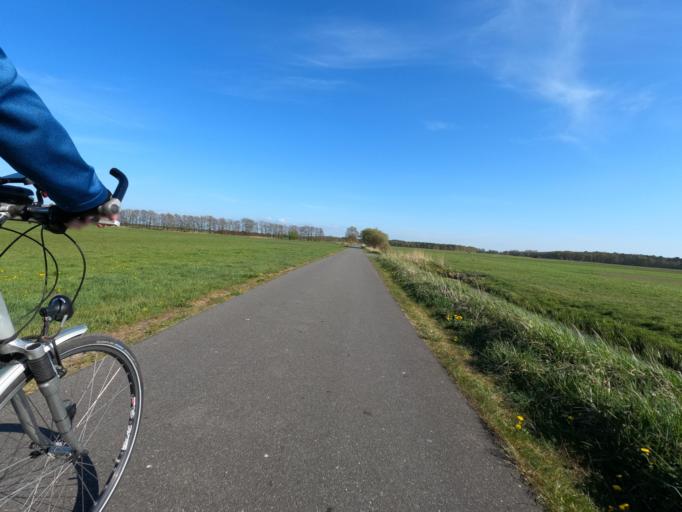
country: DE
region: Mecklenburg-Vorpommern
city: Ostseebad Prerow
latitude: 54.4401
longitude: 12.5893
